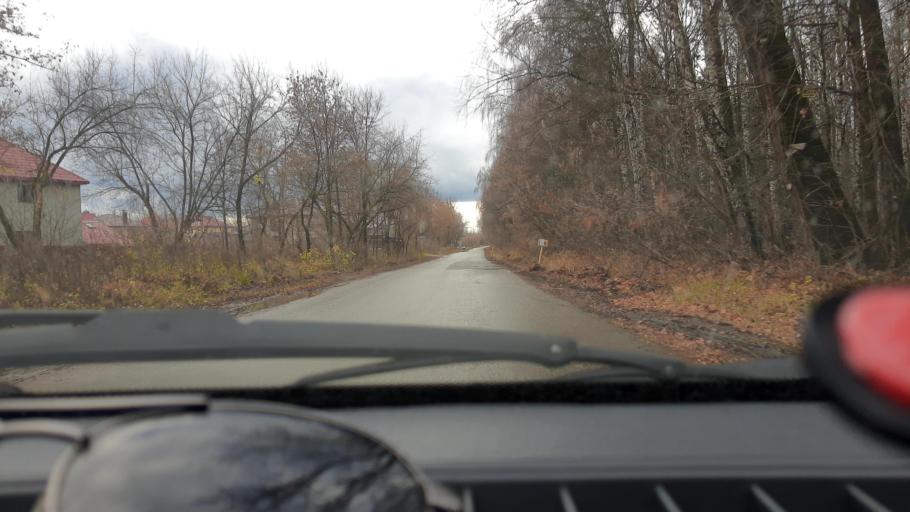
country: RU
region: Bashkortostan
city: Ufa
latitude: 54.7921
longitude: 56.1565
